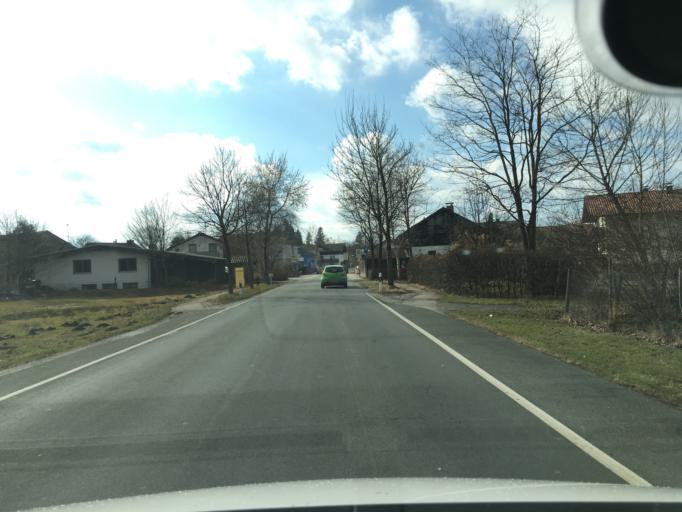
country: DE
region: Bavaria
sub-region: Upper Bavaria
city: Stephanskirchen
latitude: 47.8356
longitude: 12.1830
